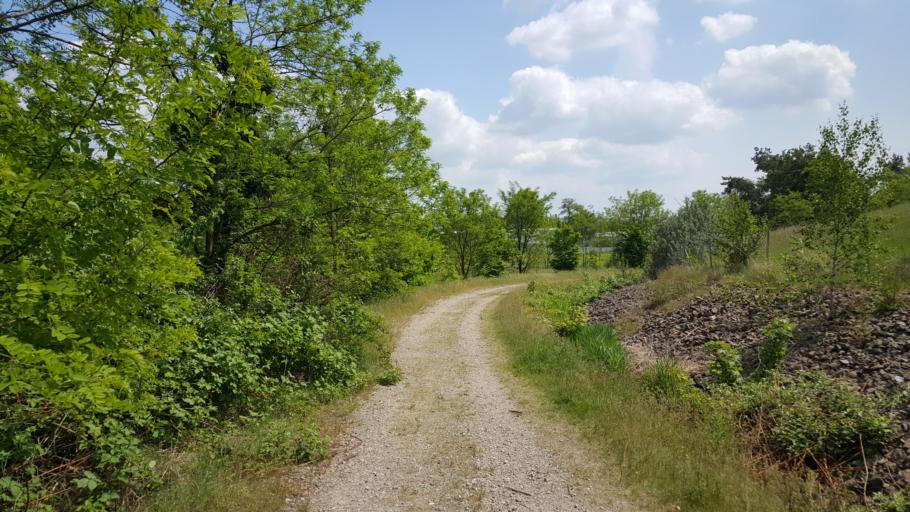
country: DE
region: Saxony
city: Albertstadt
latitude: 51.0867
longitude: 13.7551
